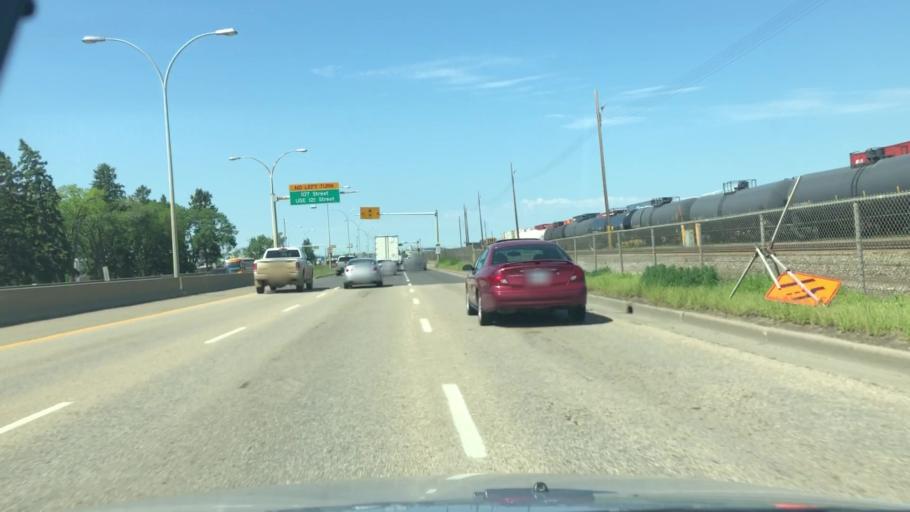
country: CA
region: Alberta
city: Edmonton
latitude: 53.5815
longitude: -113.5021
